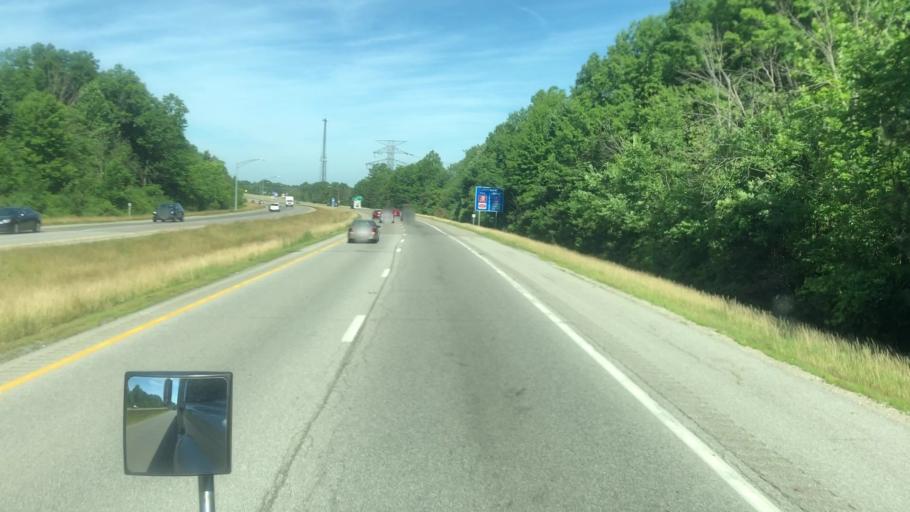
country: US
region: Ohio
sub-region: Lorain County
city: Amherst
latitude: 41.4137
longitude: -82.1974
